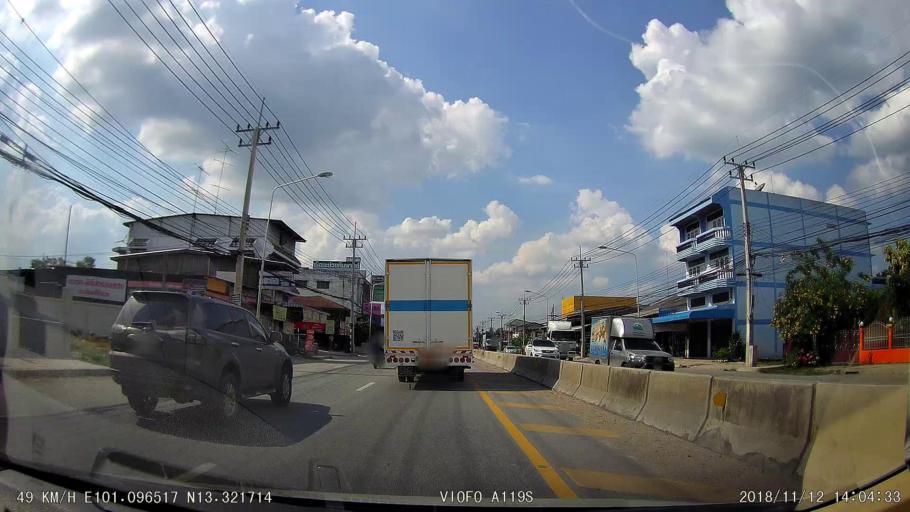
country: TH
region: Chon Buri
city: Ban Bueng
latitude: 13.3218
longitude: 101.0964
